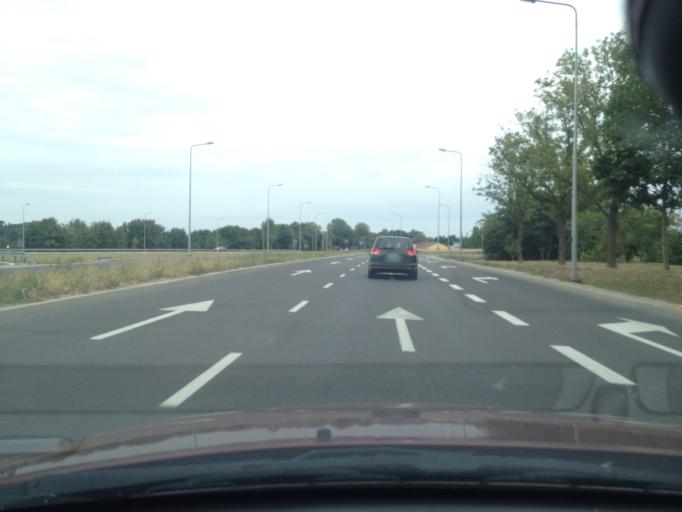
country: PL
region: Lubusz
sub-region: Powiat gorzowski
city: Klodawa
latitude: 52.7445
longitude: 15.1619
